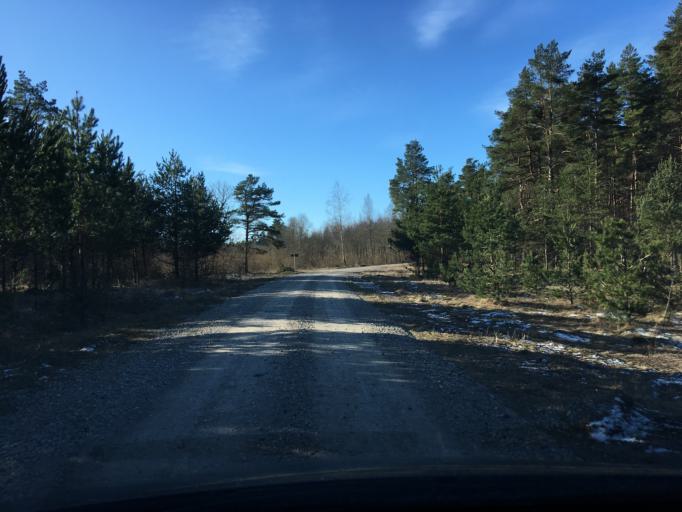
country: EE
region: Laeaene
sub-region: Lihula vald
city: Lihula
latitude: 58.5734
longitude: 23.6972
